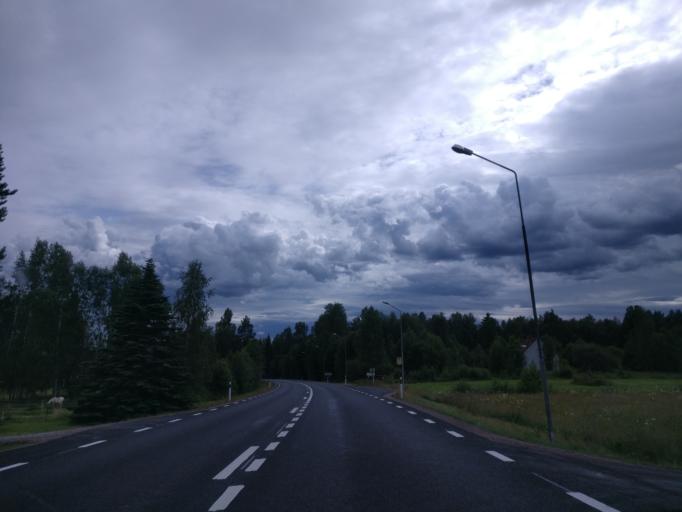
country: SE
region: Vaermland
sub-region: Hagfors Kommun
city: Ekshaerad
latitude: 60.0696
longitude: 13.5502
